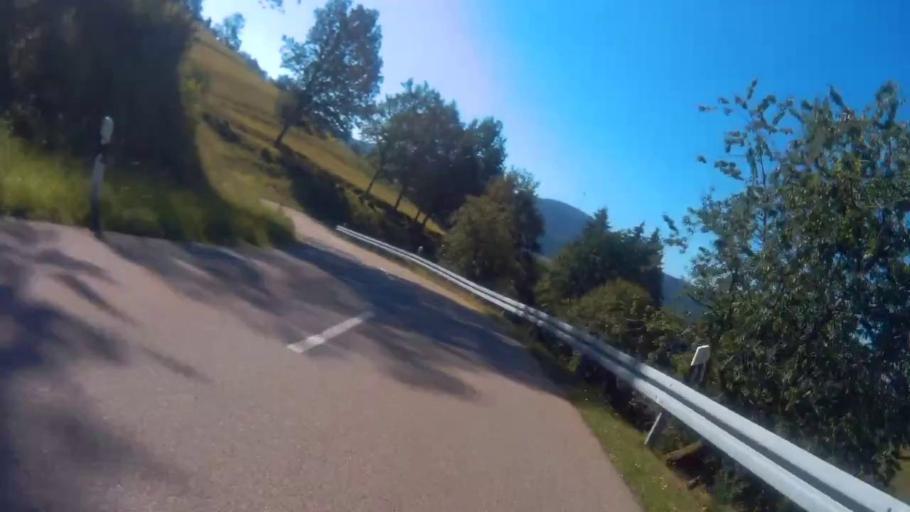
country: DE
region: Baden-Wuerttemberg
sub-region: Freiburg Region
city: Wembach
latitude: 47.7425
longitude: 7.9108
